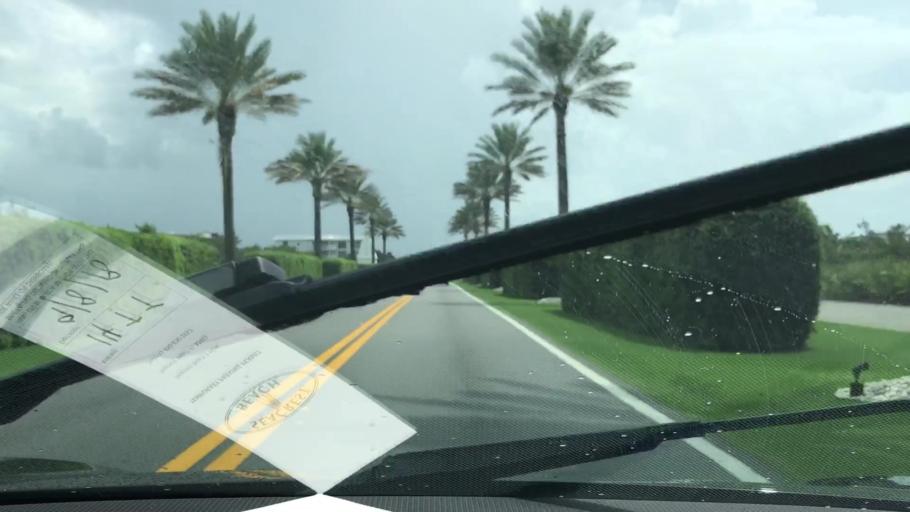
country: US
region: Florida
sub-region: Bay County
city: Laguna Beach
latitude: 30.2842
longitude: -86.0274
